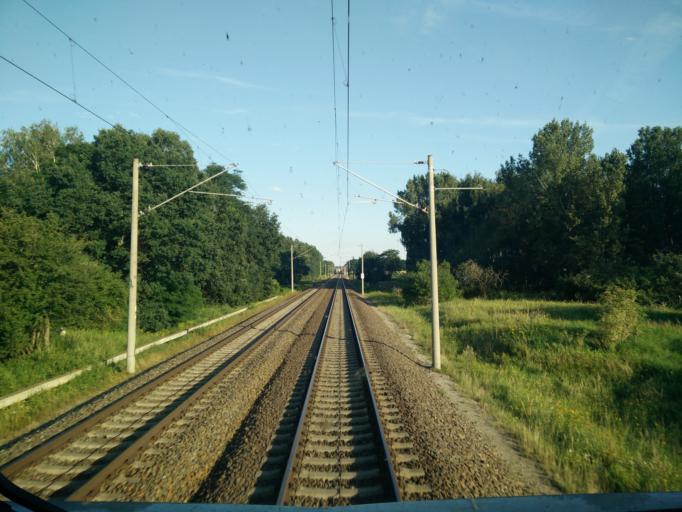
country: DE
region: Brandenburg
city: Paulinenaue
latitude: 52.6886
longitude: 12.6940
